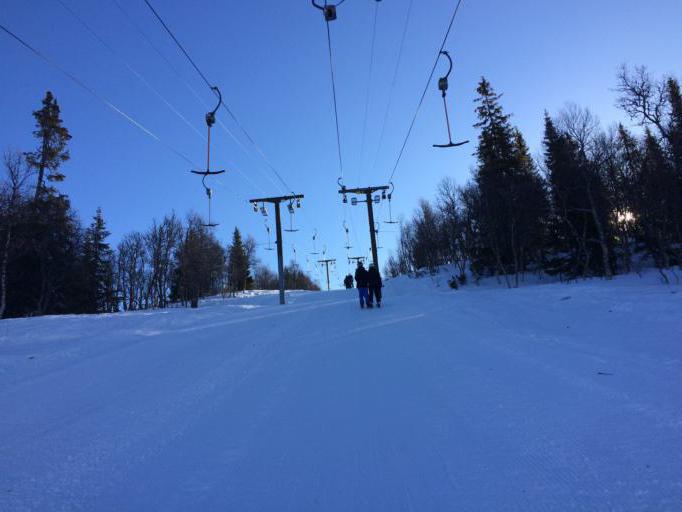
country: SE
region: Jaemtland
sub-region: Are Kommun
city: Are
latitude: 63.4304
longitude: 13.0171
